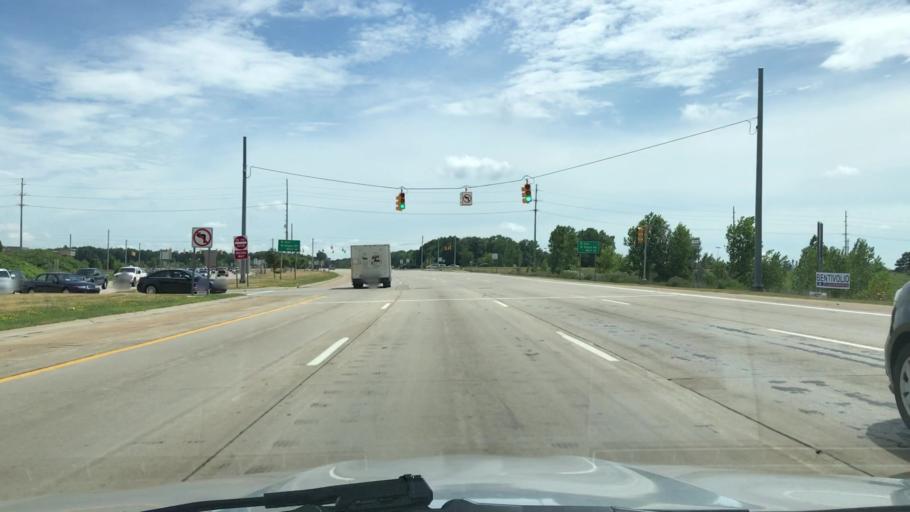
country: US
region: Michigan
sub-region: Oakland County
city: Wolverine Lake
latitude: 42.5436
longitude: -83.4518
